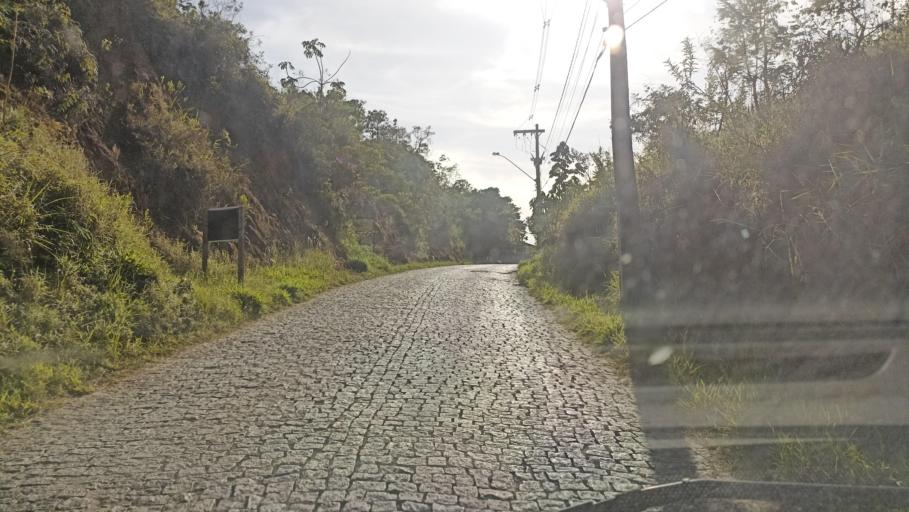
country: BR
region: Minas Gerais
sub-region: Tiradentes
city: Tiradentes
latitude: -21.1123
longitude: -44.1894
